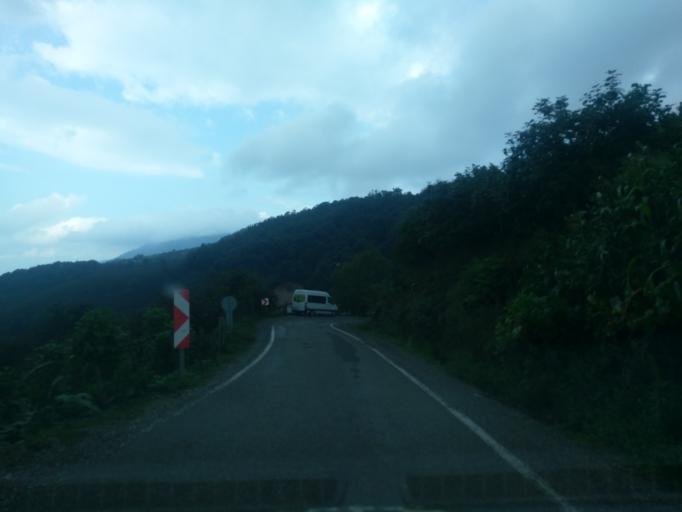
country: TR
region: Ordu
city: Gurgentepe
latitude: 40.8799
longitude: 37.6281
